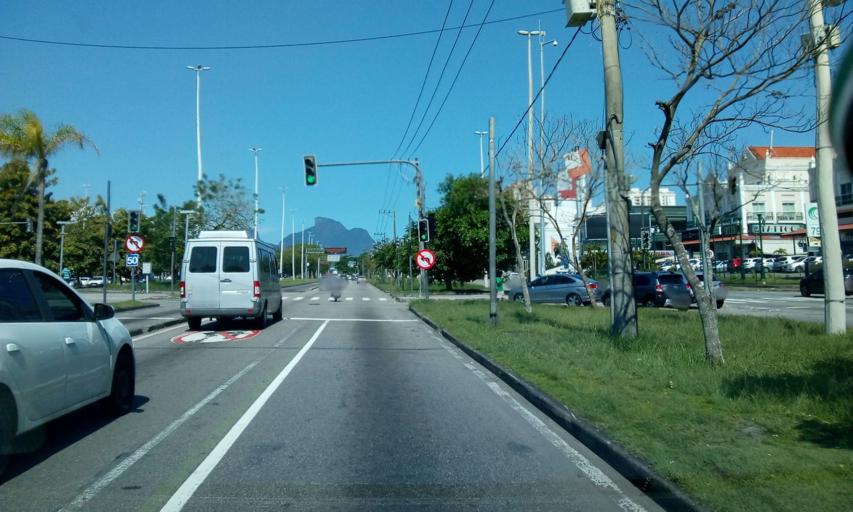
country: BR
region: Rio de Janeiro
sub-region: Nilopolis
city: Nilopolis
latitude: -23.0006
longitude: -43.3888
